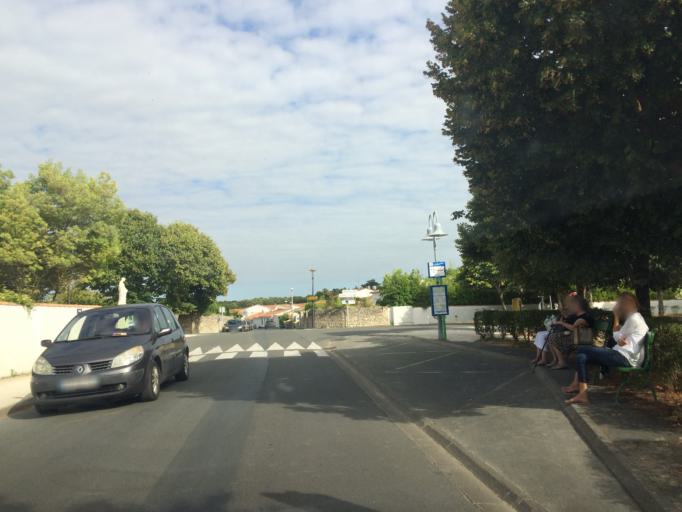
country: FR
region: Poitou-Charentes
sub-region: Departement de la Charente-Maritime
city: La Flotte
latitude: 46.1846
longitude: -1.3303
